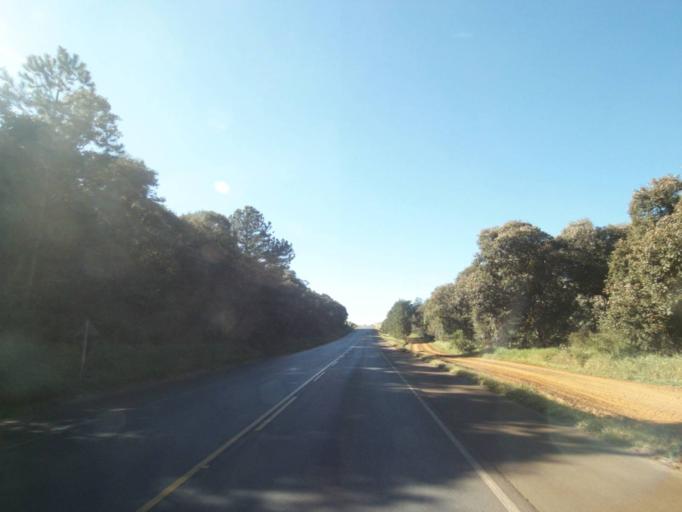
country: BR
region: Parana
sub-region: Tibagi
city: Tibagi
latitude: -24.4227
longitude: -50.3832
